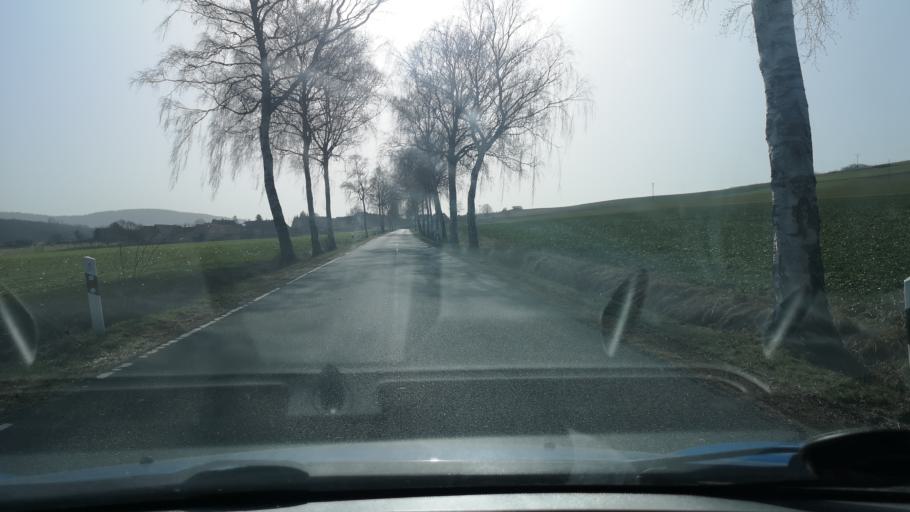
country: DE
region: Lower Saxony
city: Weenzen
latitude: 51.9968
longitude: 9.6472
